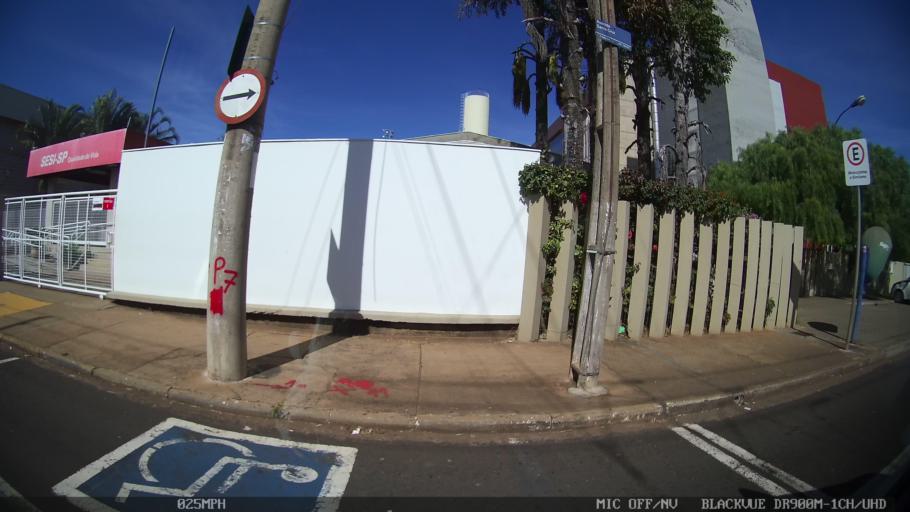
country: BR
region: Sao Paulo
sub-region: Franca
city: Franca
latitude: -20.5421
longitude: -47.3824
